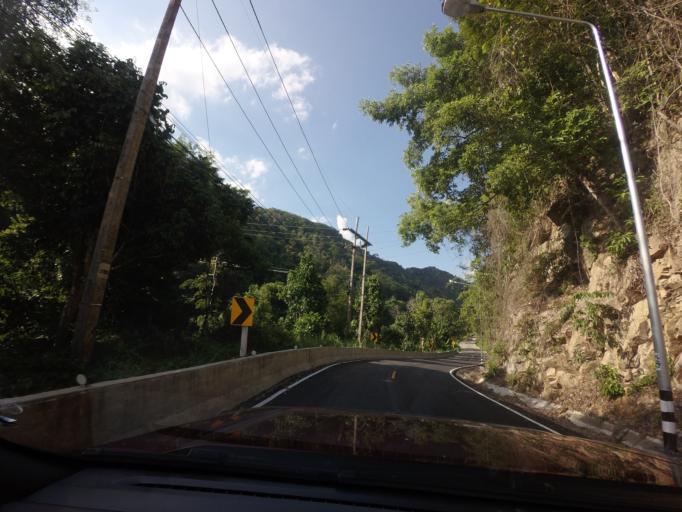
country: TH
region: Yala
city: Than To
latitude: 6.1331
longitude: 101.2985
